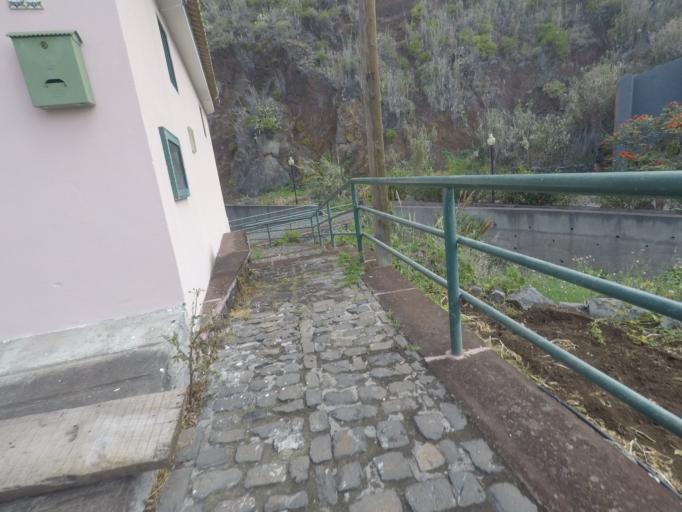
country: PT
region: Madeira
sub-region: Calheta
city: Faja da Ovelha
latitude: 32.7658
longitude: -17.2351
